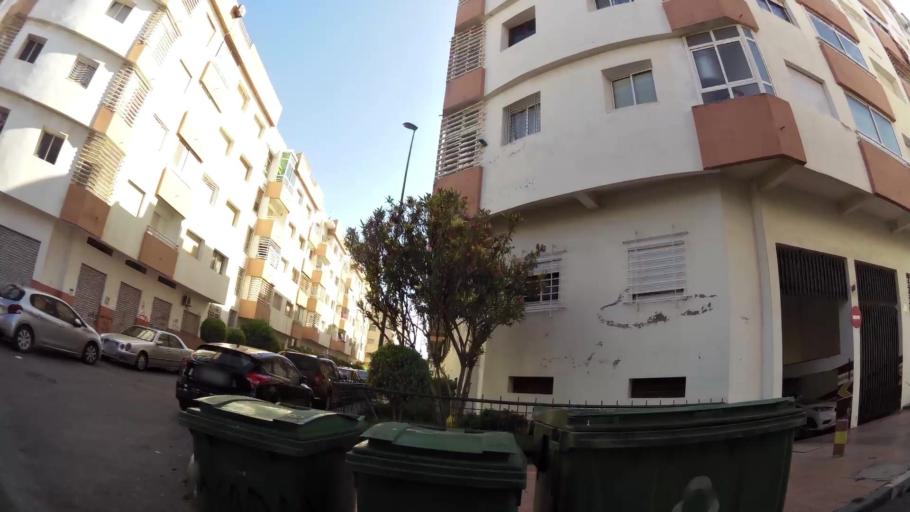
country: MA
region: Rabat-Sale-Zemmour-Zaer
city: Sale
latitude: 34.0688
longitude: -6.7944
